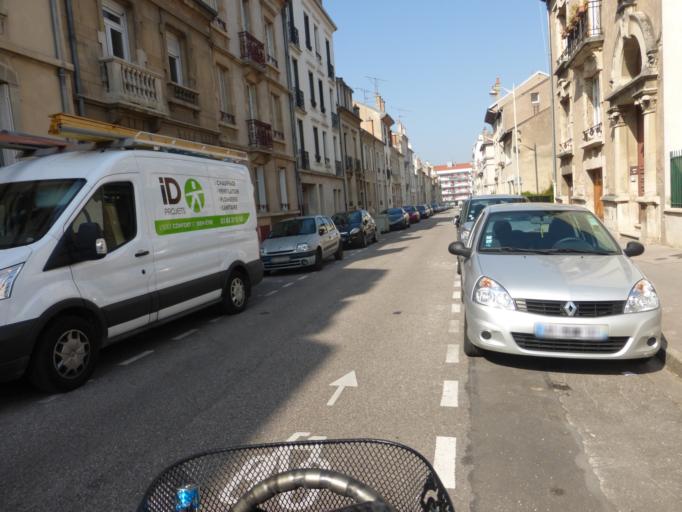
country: FR
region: Lorraine
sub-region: Departement de Meurthe-et-Moselle
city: Villers-les-Nancy
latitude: 48.6747
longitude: 6.1647
